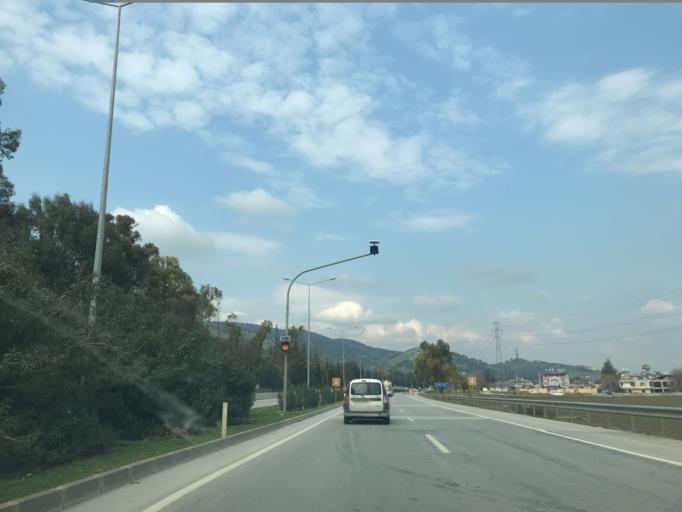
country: TR
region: Hatay
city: Serinyol
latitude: 36.3825
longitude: 36.2296
